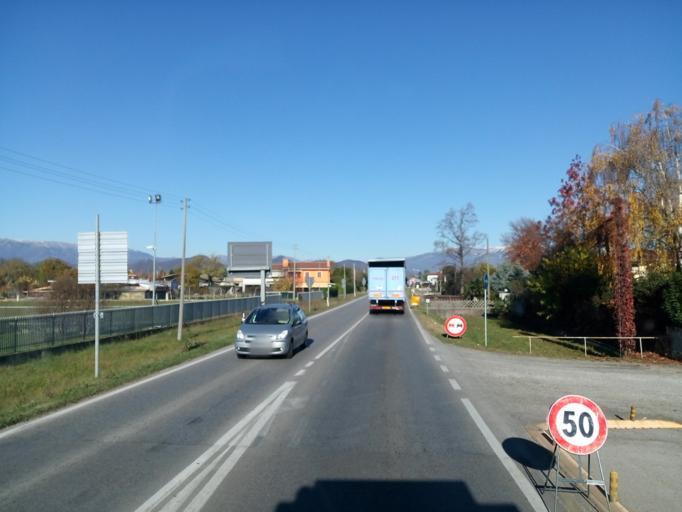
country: IT
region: Veneto
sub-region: Provincia di Treviso
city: Caerano di San Marco
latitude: 45.7639
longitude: 11.9949
